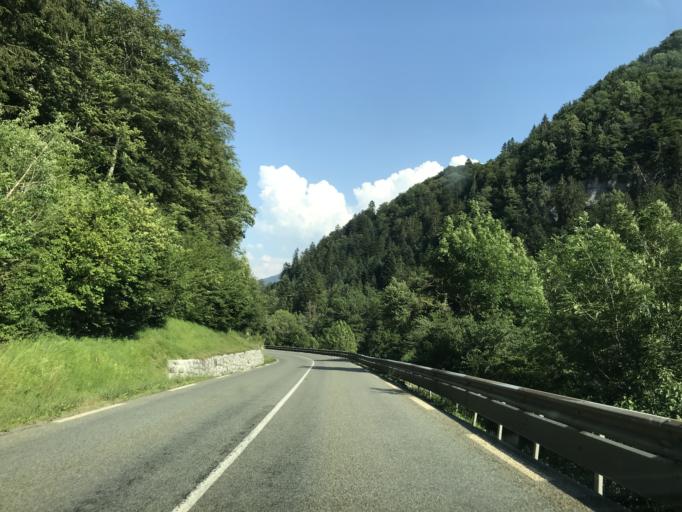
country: FR
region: Rhone-Alpes
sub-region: Departement de la Haute-Savoie
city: Thyez
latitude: 46.1116
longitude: 6.5555
